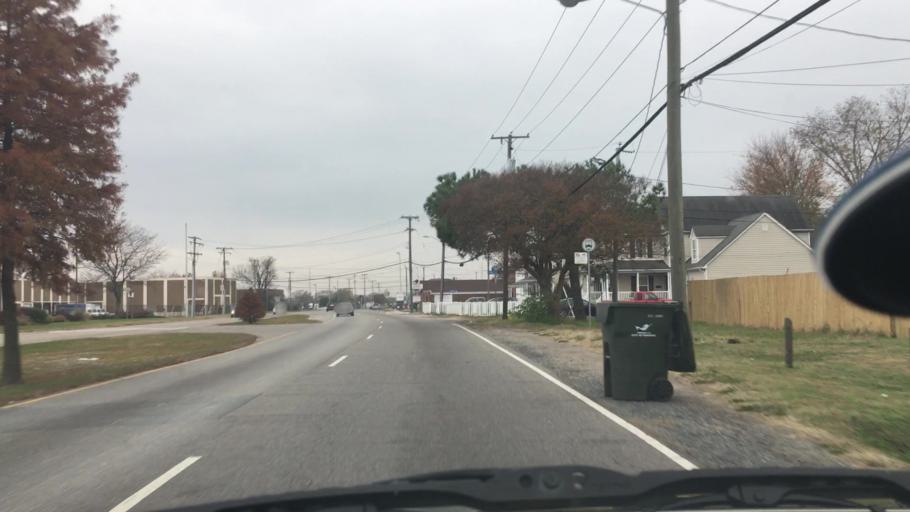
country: US
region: Virginia
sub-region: City of Norfolk
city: Norfolk
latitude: 36.8649
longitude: -76.2403
